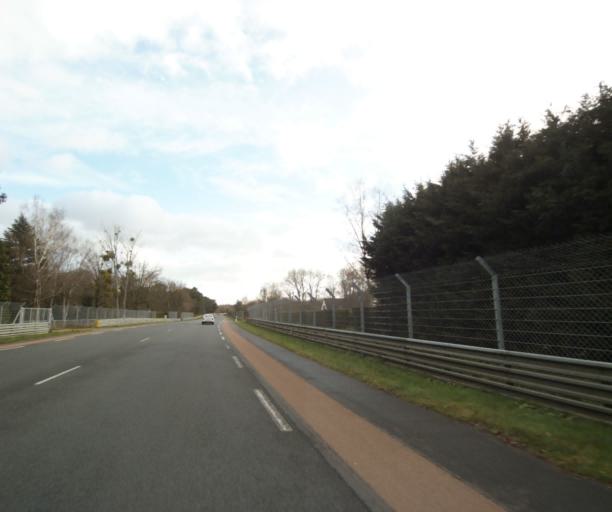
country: FR
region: Pays de la Loire
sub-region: Departement de la Sarthe
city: Arnage
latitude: 47.9303
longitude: 0.2109
